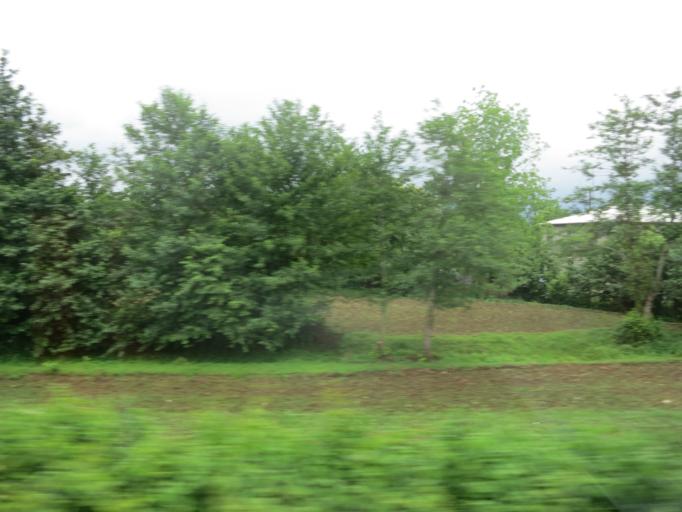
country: GE
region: Ajaria
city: Kobuleti
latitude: 41.8002
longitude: 41.7744
